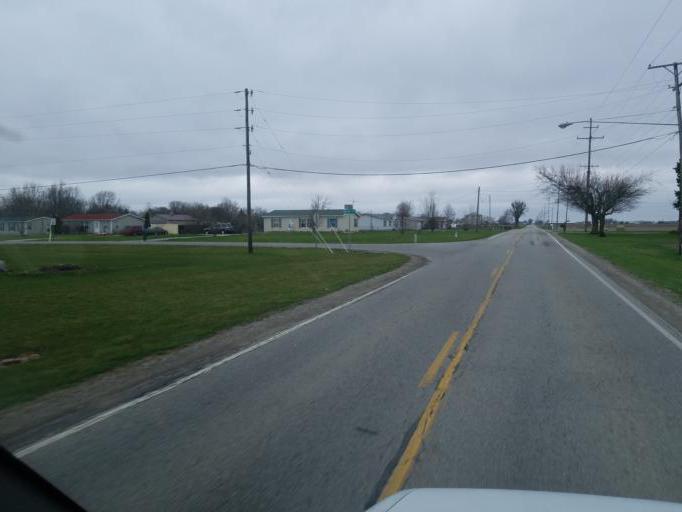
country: US
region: Ohio
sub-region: Marion County
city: Marion
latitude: 40.6389
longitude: -83.0732
